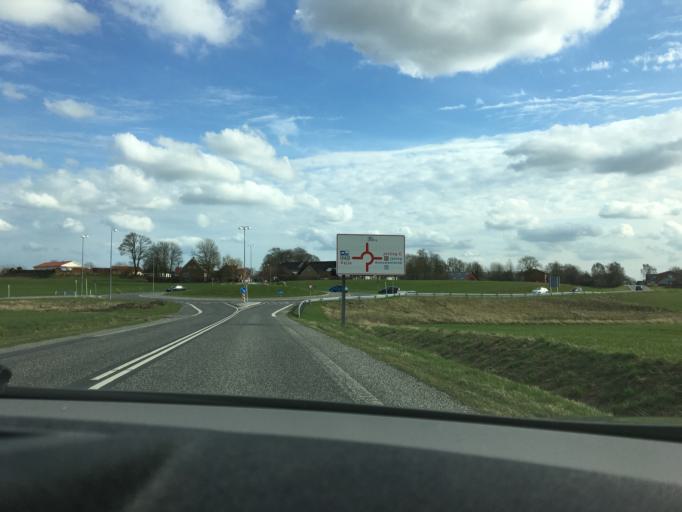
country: DK
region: South Denmark
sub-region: Vejle Kommune
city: Jelling
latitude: 55.7601
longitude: 9.4139
